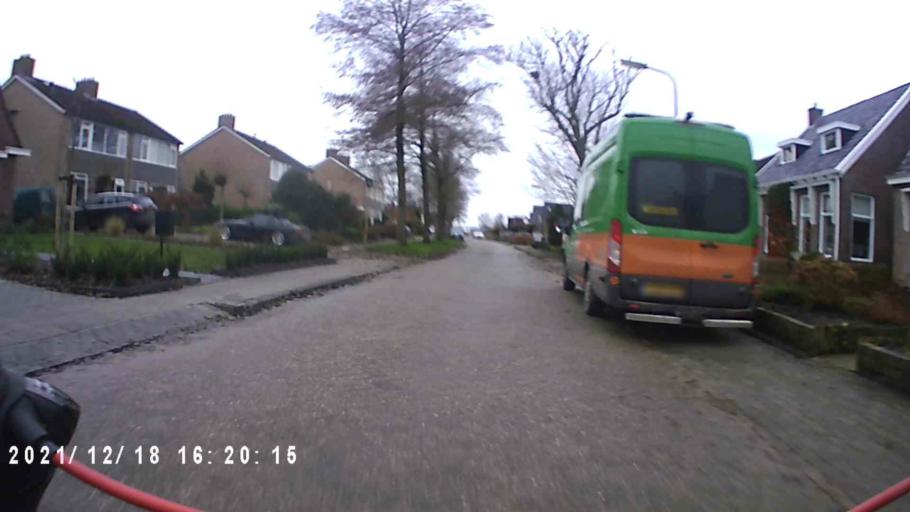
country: NL
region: Friesland
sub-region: Gemeente Dongeradeel
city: Anjum
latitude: 53.3793
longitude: 6.0520
